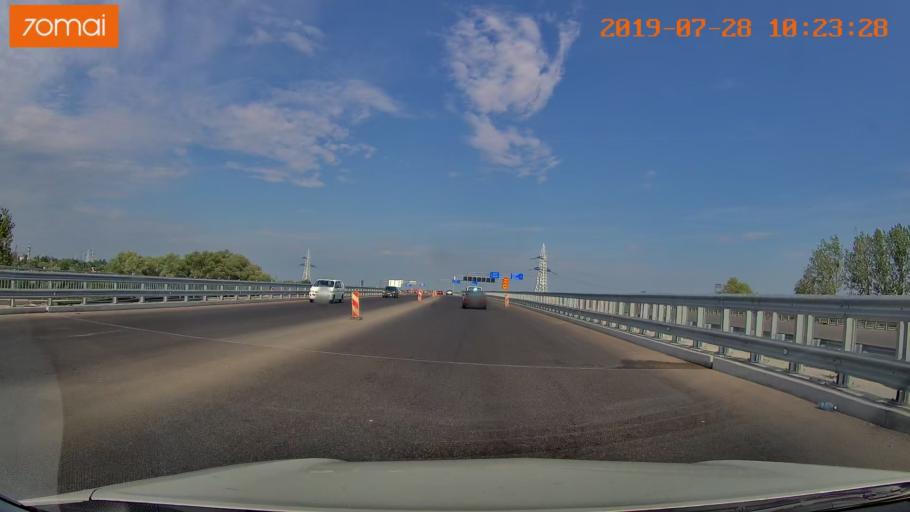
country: RU
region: Kaliningrad
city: Maloye Isakovo
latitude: 54.7667
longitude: 20.5589
